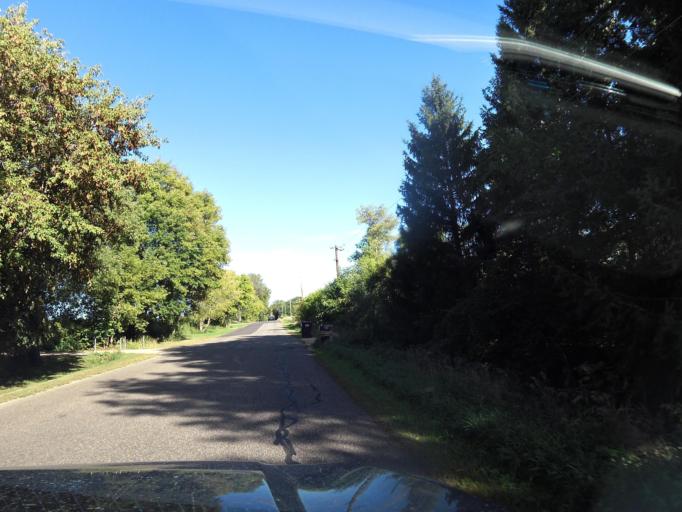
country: US
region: Minnesota
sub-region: Washington County
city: Afton
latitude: 44.8762
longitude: -92.8332
